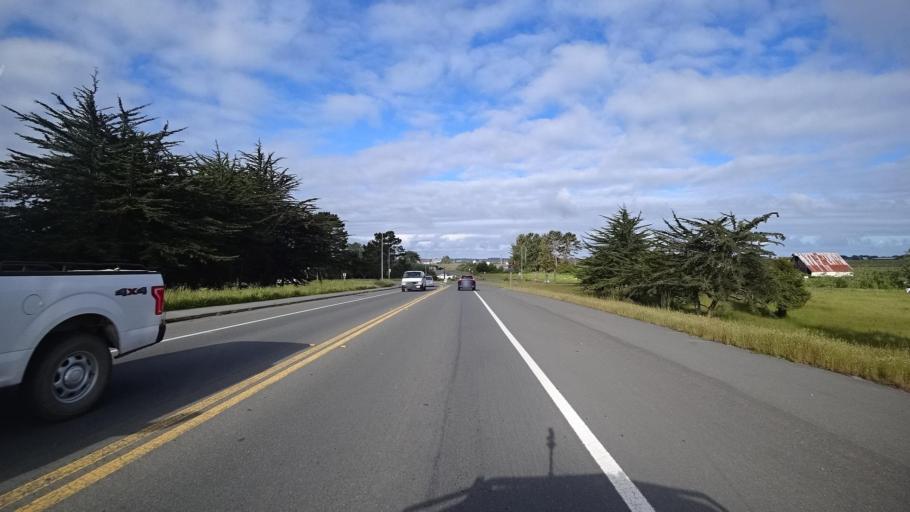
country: US
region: California
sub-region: Humboldt County
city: Arcata
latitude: 40.9042
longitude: -124.0880
